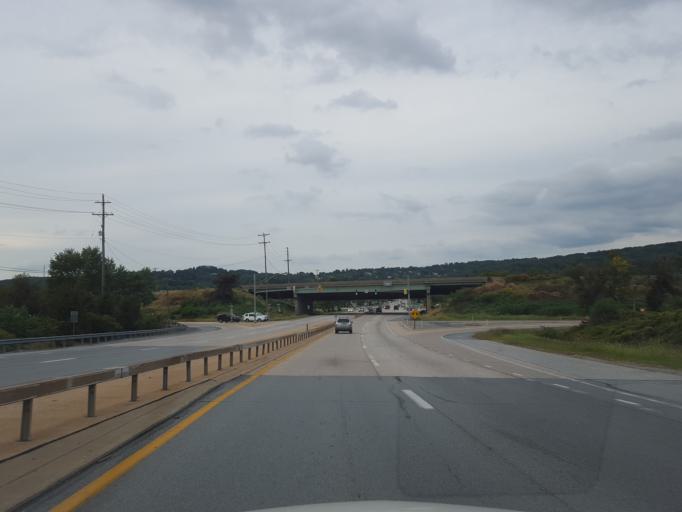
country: US
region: Pennsylvania
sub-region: York County
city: Yorklyn
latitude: 39.9847
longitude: -76.6662
